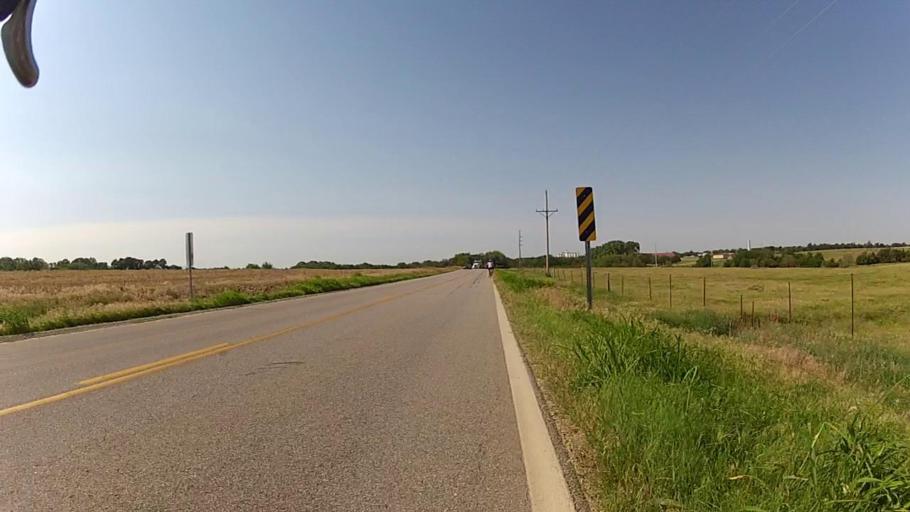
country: US
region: Kansas
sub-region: Sumner County
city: Caldwell
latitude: 37.0485
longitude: -97.6008
